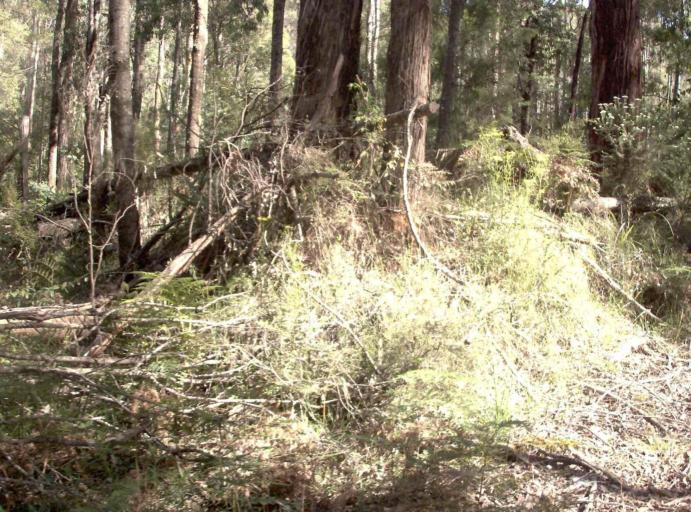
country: AU
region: Victoria
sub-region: East Gippsland
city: Lakes Entrance
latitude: -37.3951
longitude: 148.5948
